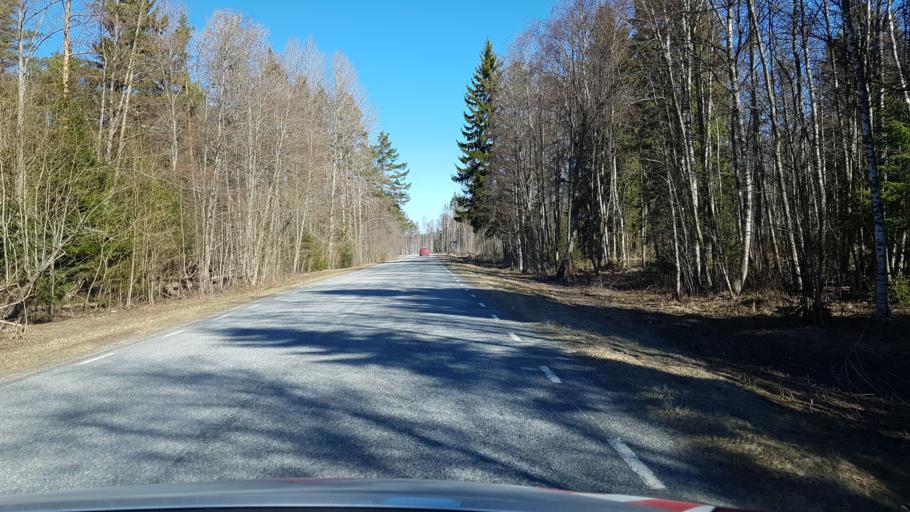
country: EE
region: Laeaene-Virumaa
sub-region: Haljala vald
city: Haljala
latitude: 59.4812
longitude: 26.2479
